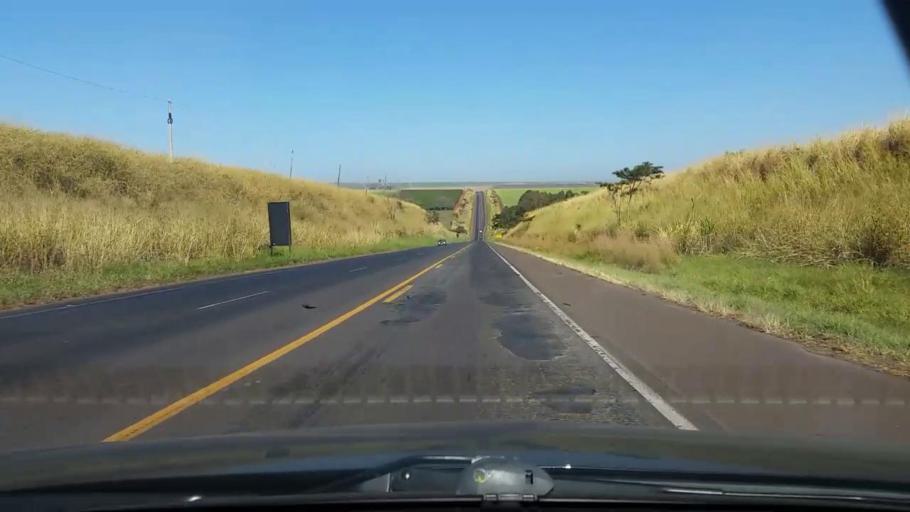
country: BR
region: Sao Paulo
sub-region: Jau
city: Jau
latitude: -22.3433
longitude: -48.5724
